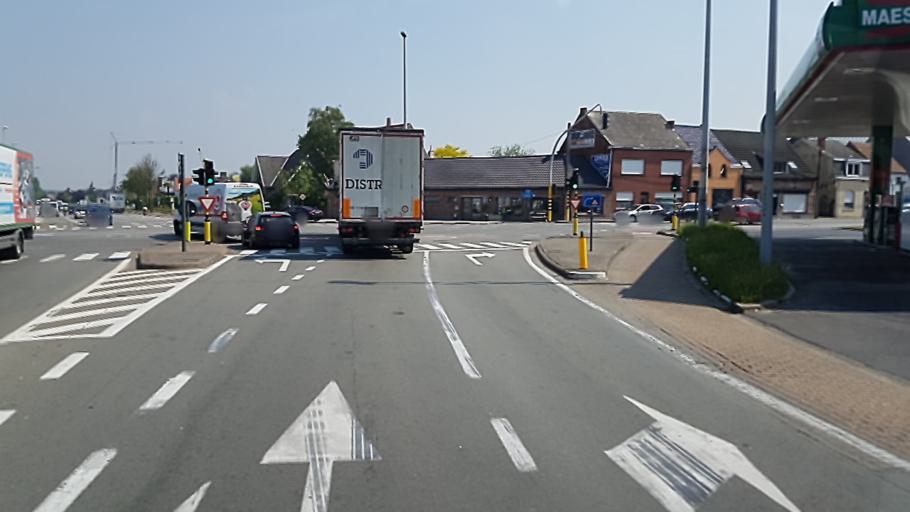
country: BE
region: Flanders
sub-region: Provincie Oost-Vlaanderen
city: Melle
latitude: 50.9840
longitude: 3.8448
